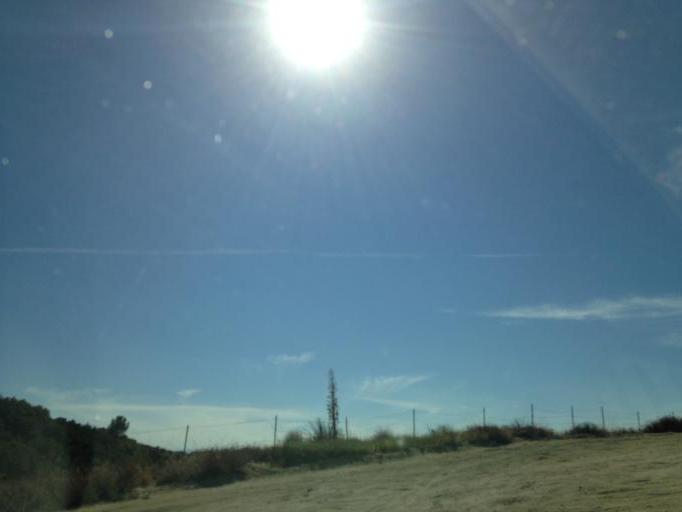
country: US
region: California
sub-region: San Bernardino County
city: Running Springs
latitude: 34.1698
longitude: -117.0953
